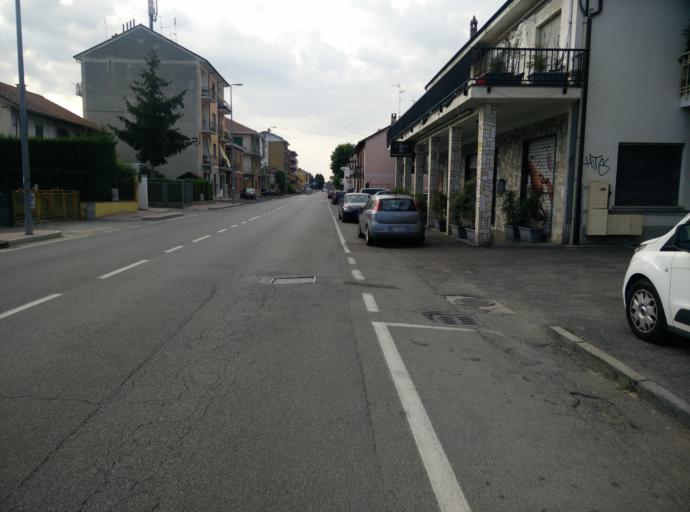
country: IT
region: Piedmont
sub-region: Provincia di Torino
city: Moncalieri
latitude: 44.9926
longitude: 7.7145
